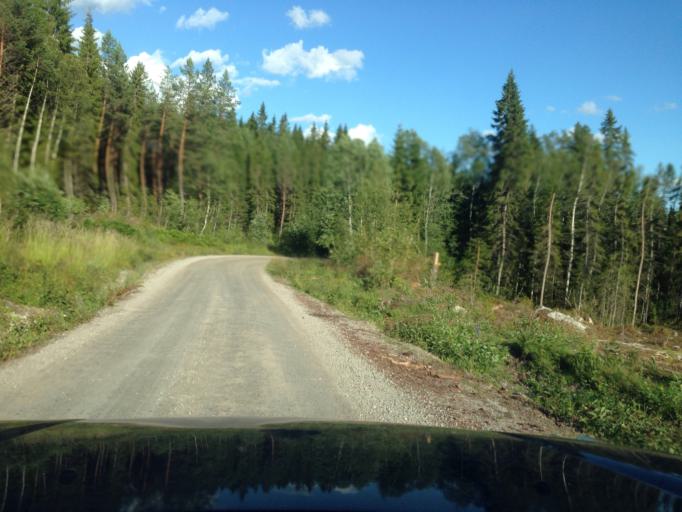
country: SE
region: Dalarna
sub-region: Ludvika Kommun
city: Abborrberget
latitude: 60.2356
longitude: 14.8033
